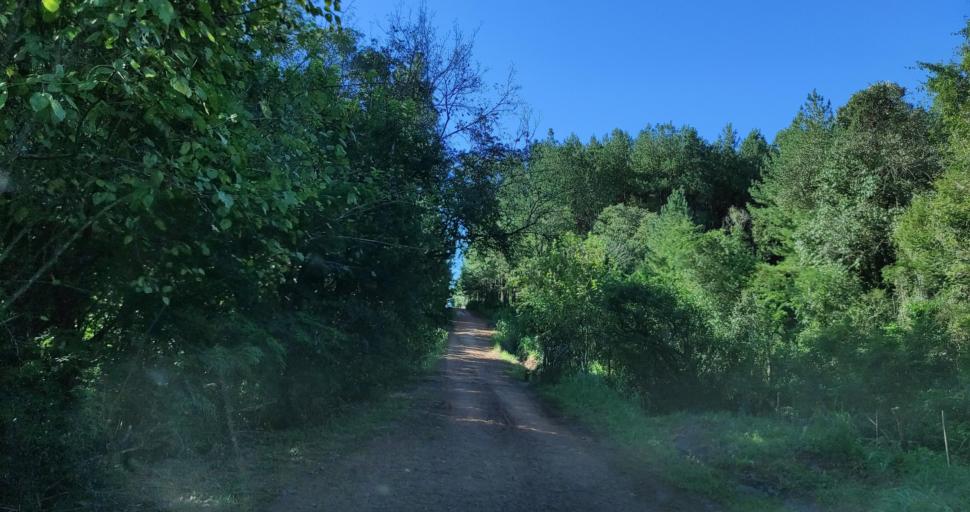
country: AR
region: Misiones
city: Capiovi
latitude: -26.9279
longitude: -55.0010
